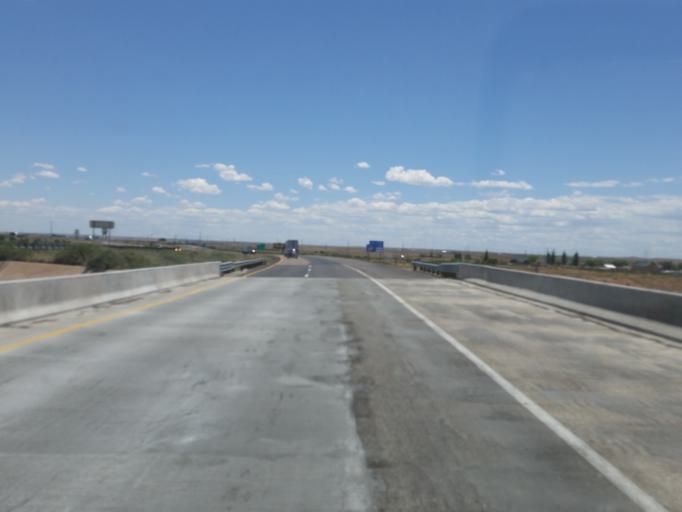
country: US
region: Arizona
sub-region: Navajo County
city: Winslow
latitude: 35.0244
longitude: -110.6820
